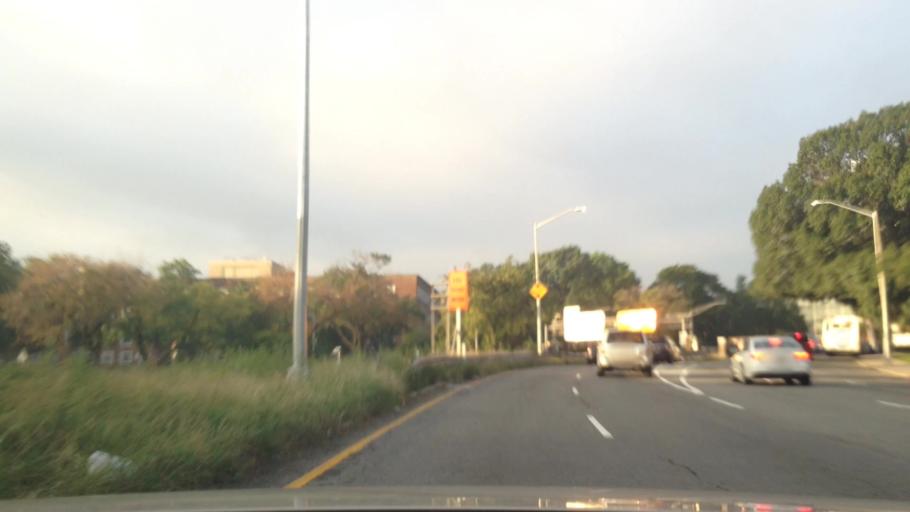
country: US
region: New York
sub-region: Queens County
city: Jamaica
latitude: 40.7157
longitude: -73.8284
